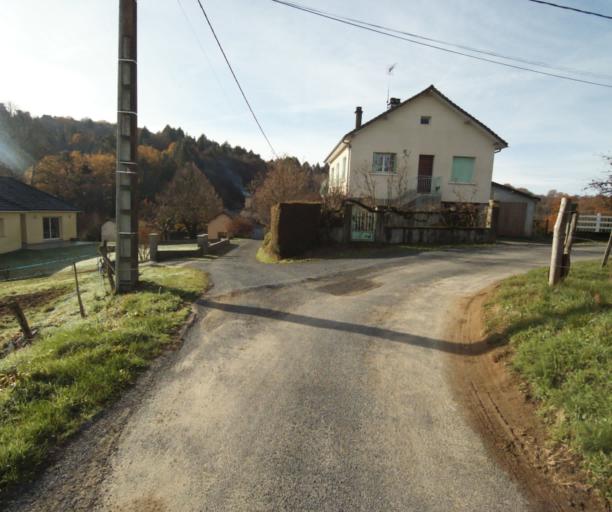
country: FR
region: Limousin
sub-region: Departement de la Correze
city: Sainte-Fortunade
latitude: 45.2207
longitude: 1.7396
